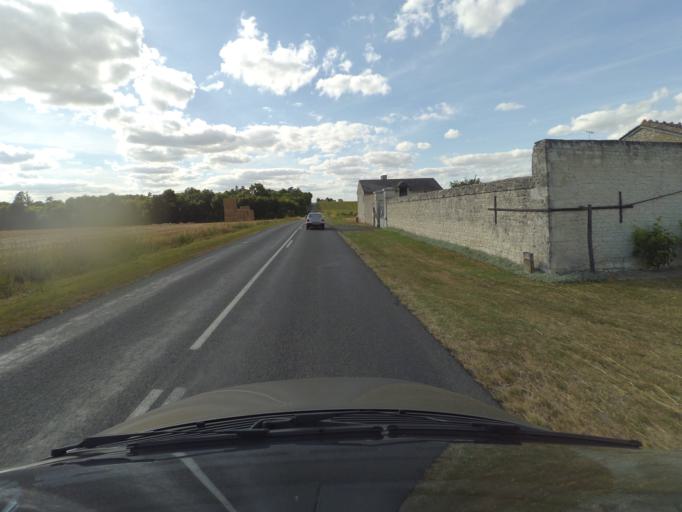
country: FR
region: Poitou-Charentes
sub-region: Departement de la Vienne
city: Saint-Gervais-les-Trois-Clochers
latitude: 46.9552
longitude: 0.4007
